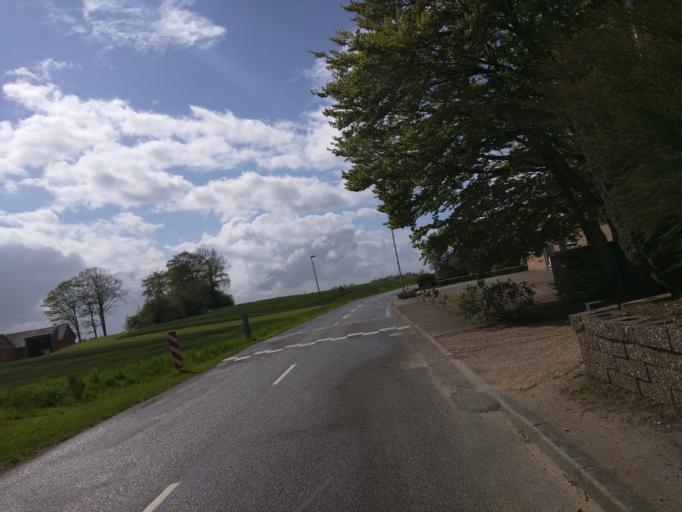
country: DK
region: Central Jutland
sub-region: Silkeborg Kommune
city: Kjellerup
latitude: 56.2756
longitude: 9.5122
